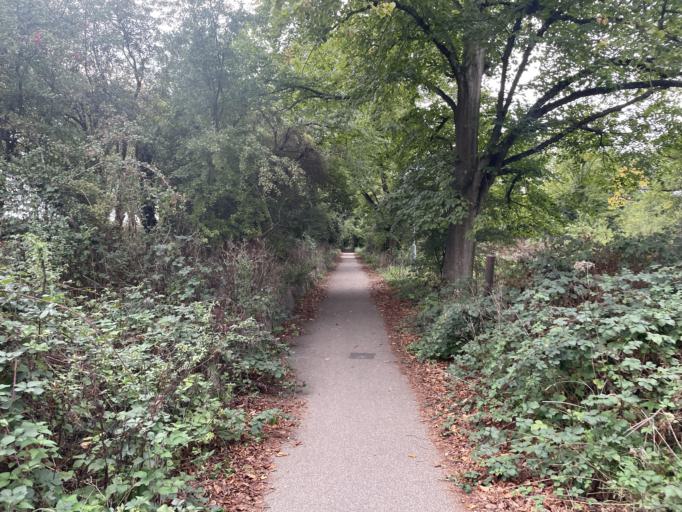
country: GB
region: England
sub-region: Hertfordshire
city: Hatfield
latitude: 51.7756
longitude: -0.2215
